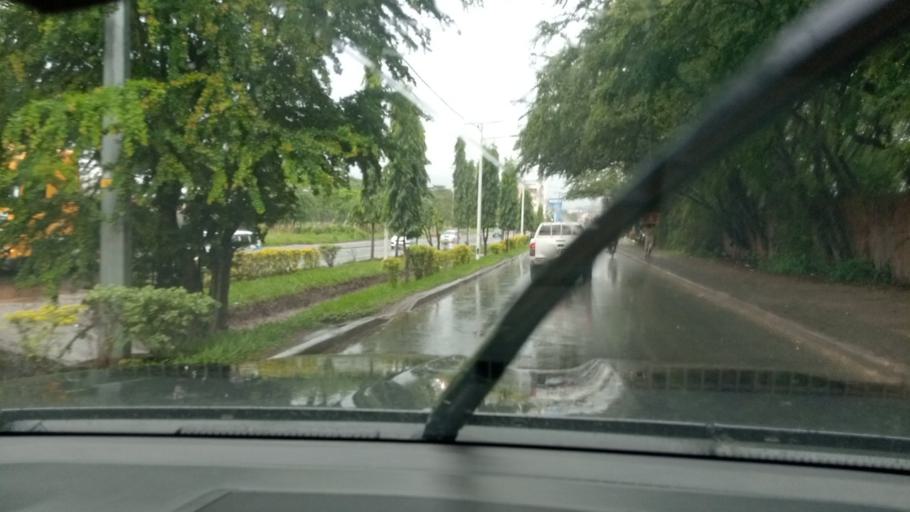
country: BI
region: Bujumbura Mairie
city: Bujumbura
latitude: -3.3771
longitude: 29.3522
